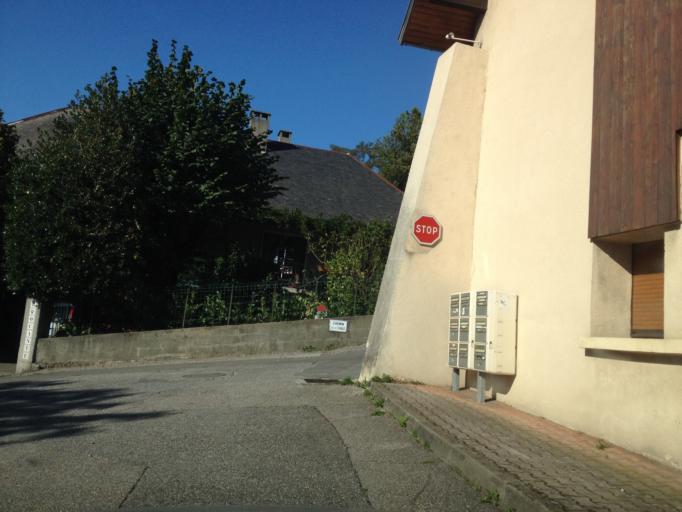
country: FR
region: Rhone-Alpes
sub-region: Departement de la Savoie
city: Voglans
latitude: 45.6295
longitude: 5.8951
